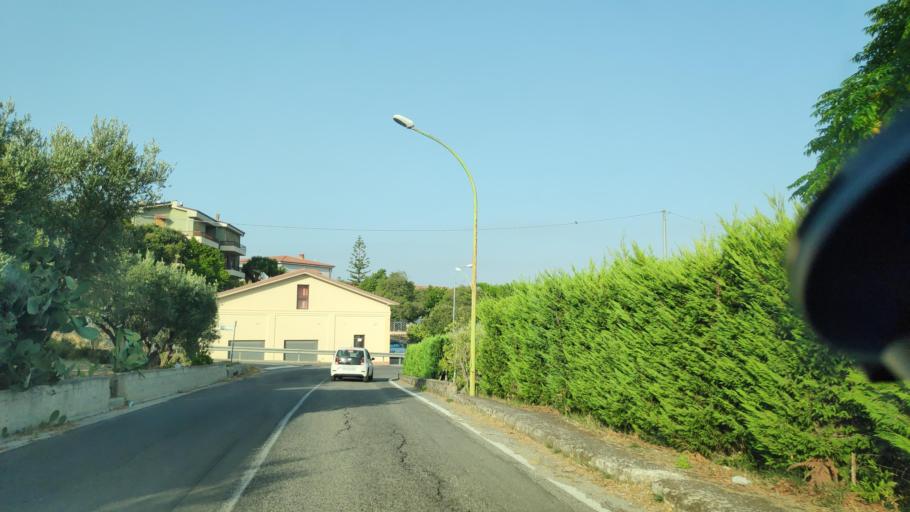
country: IT
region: Calabria
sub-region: Provincia di Catanzaro
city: Sant'Andrea Ionio Marina
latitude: 38.6199
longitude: 16.5476
